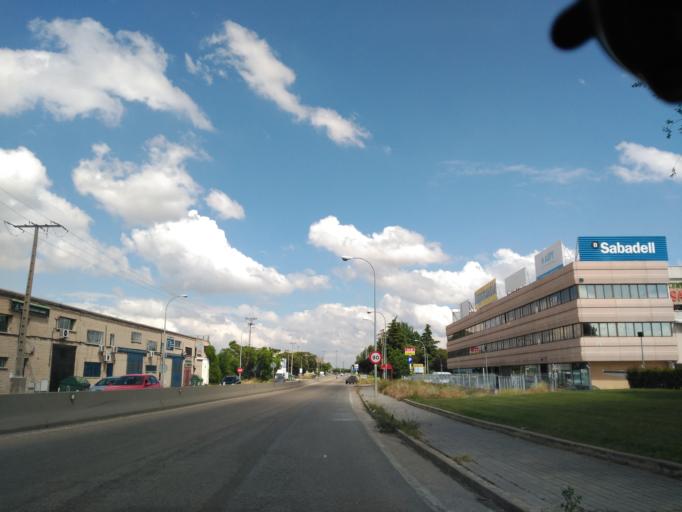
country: ES
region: Madrid
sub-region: Provincia de Madrid
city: Getafe
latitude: 40.3042
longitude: -3.7010
